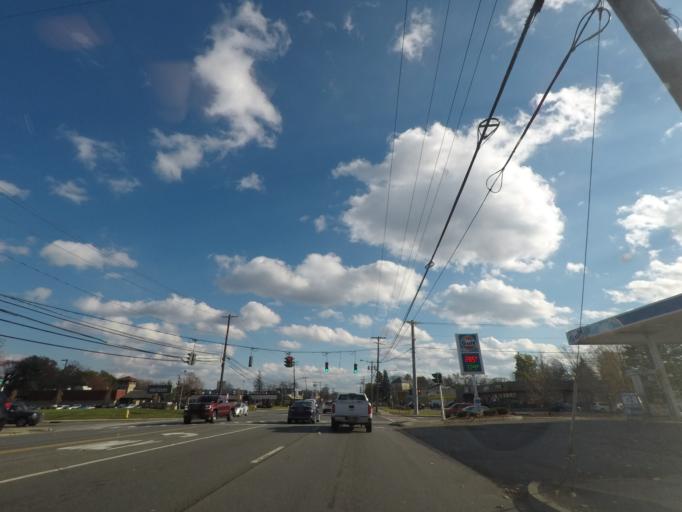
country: US
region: New York
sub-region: Albany County
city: Colonie
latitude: 42.7158
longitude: -73.8309
